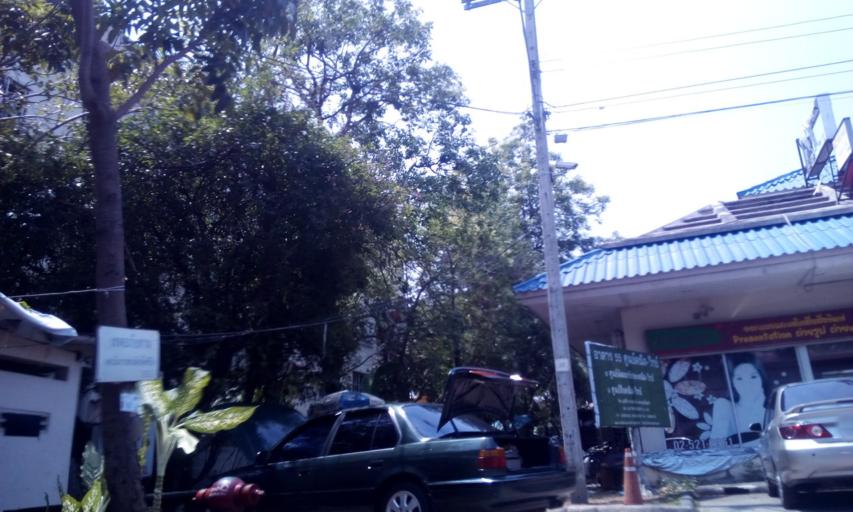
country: TH
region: Bangkok
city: Lak Si
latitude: 13.8735
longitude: 100.5912
